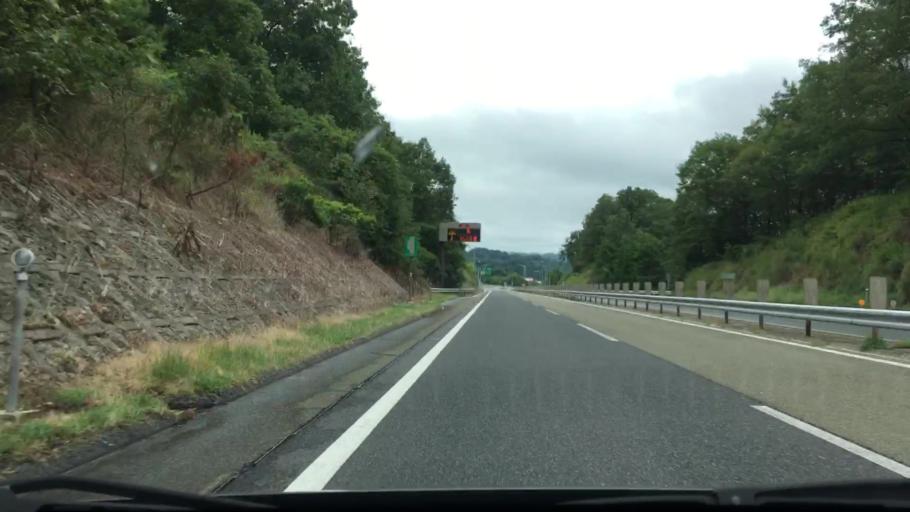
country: JP
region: Hiroshima
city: Shobara
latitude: 34.8444
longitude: 133.0302
